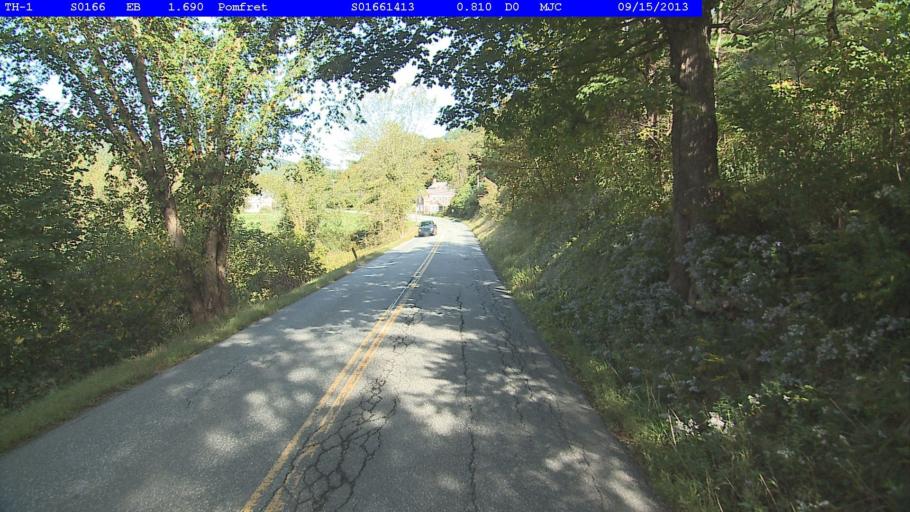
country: US
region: Vermont
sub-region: Windsor County
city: Woodstock
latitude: 43.6610
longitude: -72.5346
